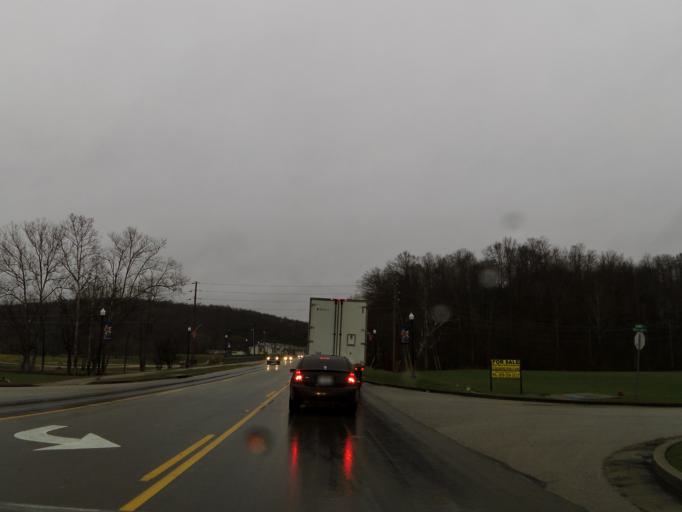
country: US
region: Kentucky
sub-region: Rockcastle County
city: Mount Vernon
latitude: 37.3858
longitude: -84.3314
